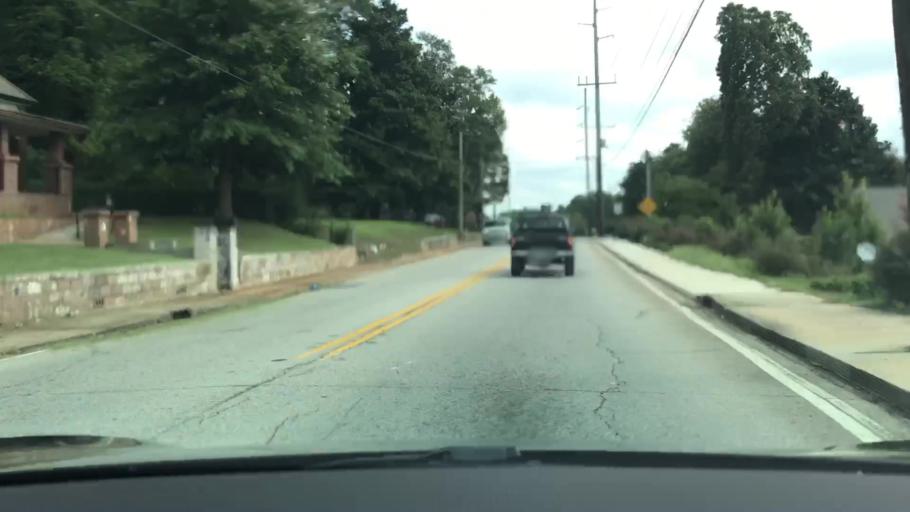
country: US
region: Georgia
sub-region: Hall County
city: Gainesville
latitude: 34.2975
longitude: -83.8137
